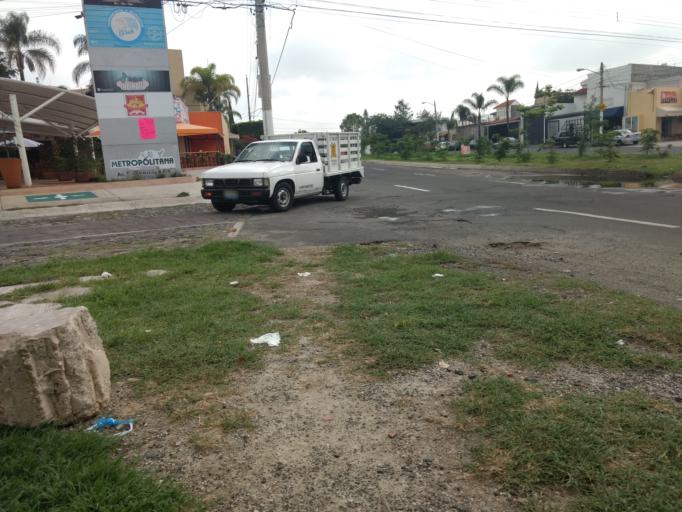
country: MX
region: Jalisco
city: Guadalajara
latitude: 20.6646
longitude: -103.4370
